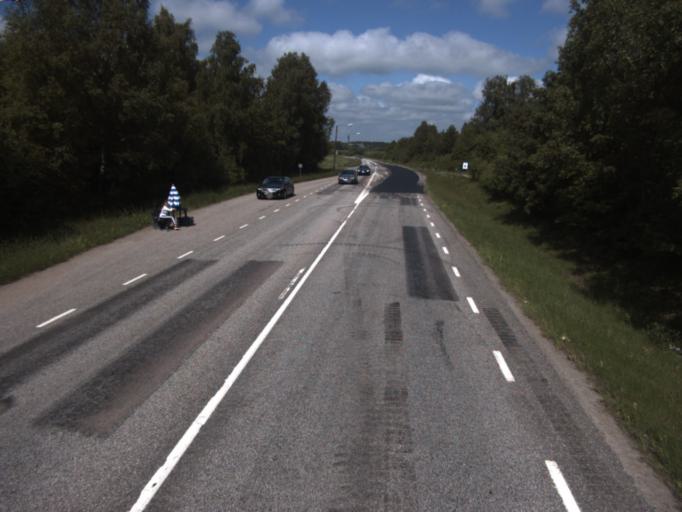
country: SE
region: Skane
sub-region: Helsingborg
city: Odakra
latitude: 56.0795
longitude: 12.7645
